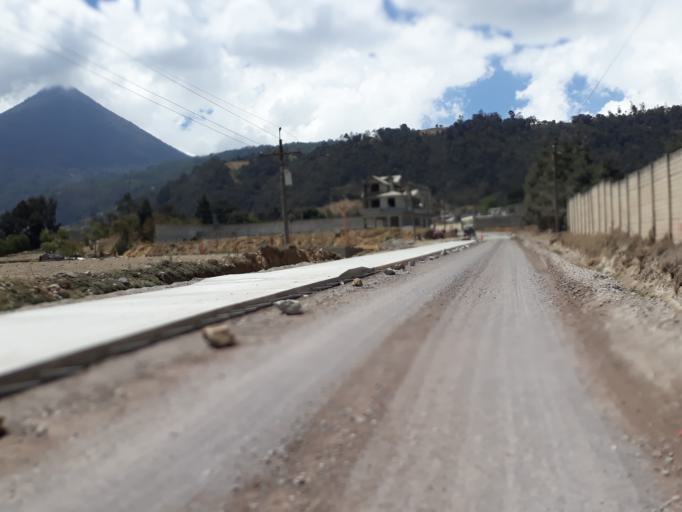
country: GT
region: Quetzaltenango
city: Quetzaltenango
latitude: 14.8095
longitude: -91.5516
